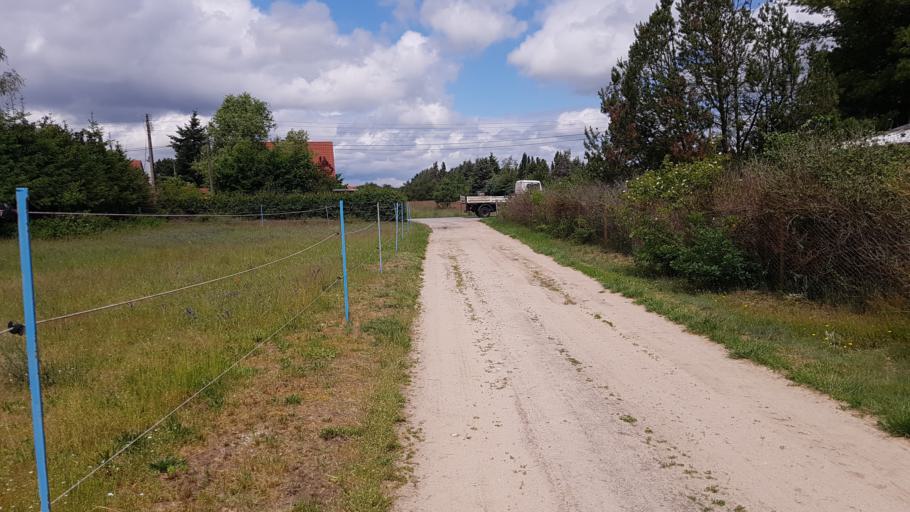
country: DE
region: Brandenburg
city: Finsterwalde
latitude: 51.6154
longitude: 13.7283
